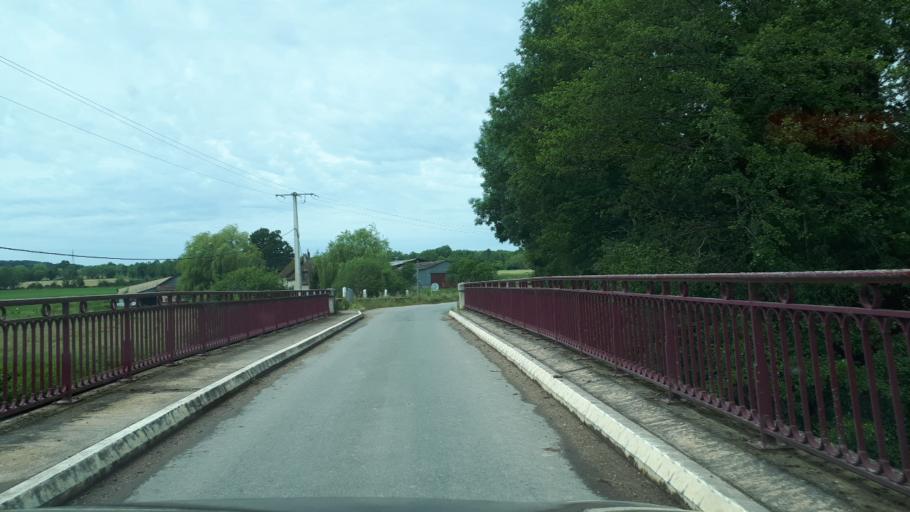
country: FR
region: Centre
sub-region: Departement du Cher
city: Savigny-en-Sancerre
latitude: 47.3958
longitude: 2.6588
